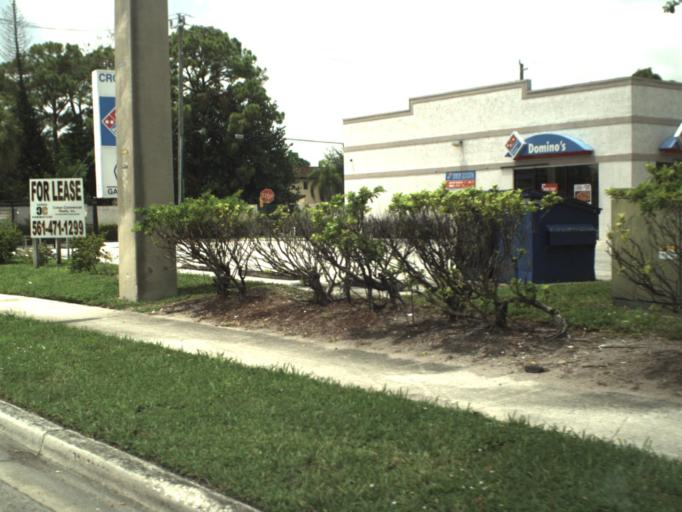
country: US
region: Florida
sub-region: Palm Beach County
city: Greenacres City
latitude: 26.6180
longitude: -80.1468
